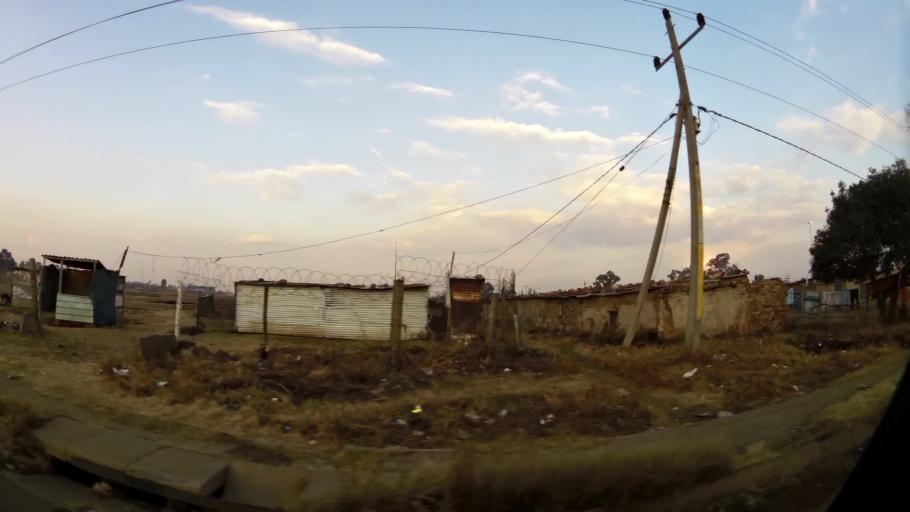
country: ZA
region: Gauteng
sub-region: City of Johannesburg Metropolitan Municipality
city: Orange Farm
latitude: -26.5438
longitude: 27.8434
